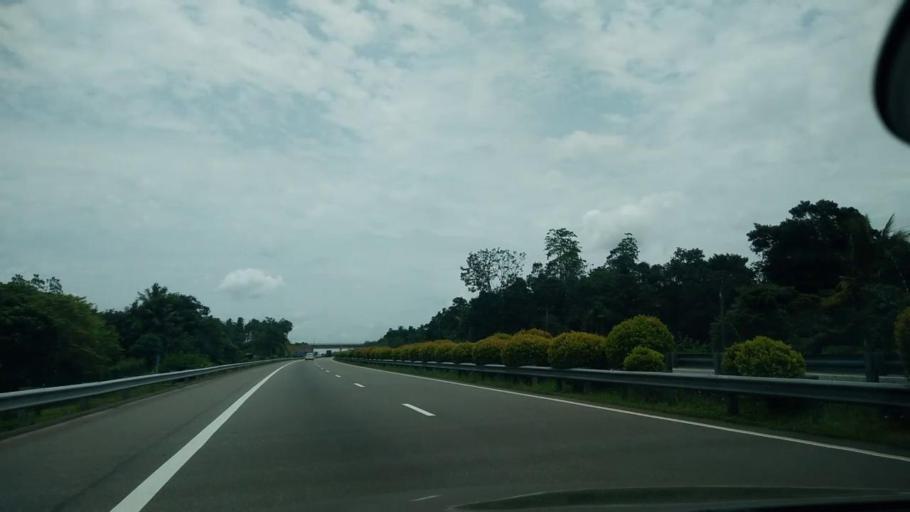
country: LK
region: Western
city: Homagama
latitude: 6.8589
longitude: 79.9777
